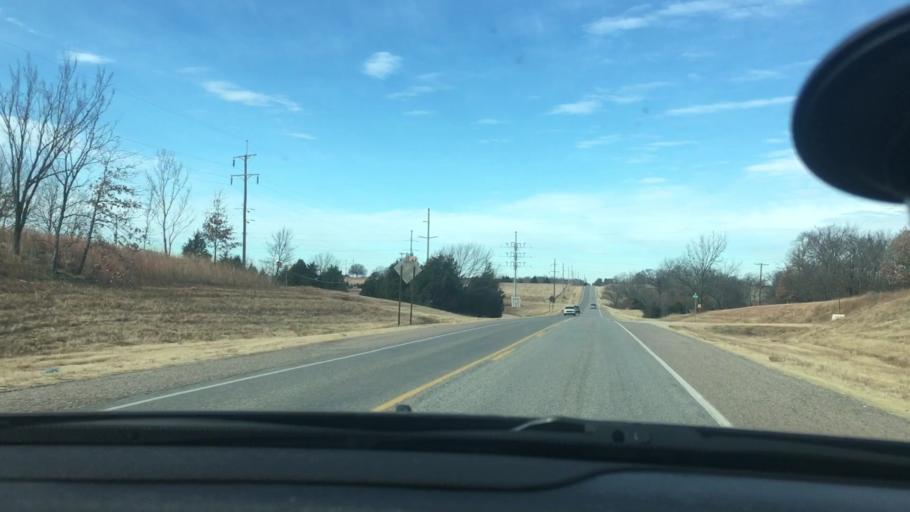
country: US
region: Oklahoma
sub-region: Seminole County
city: Konawa
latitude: 34.9418
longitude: -96.6866
